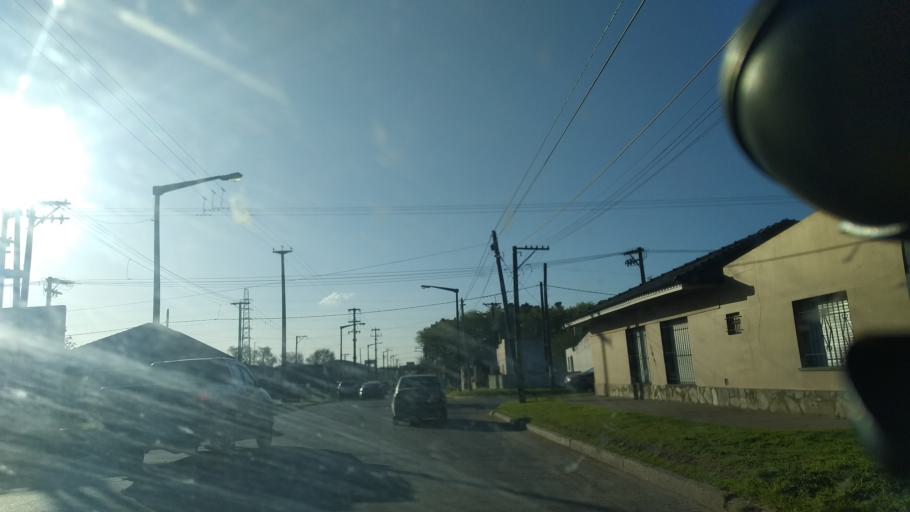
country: AR
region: Buenos Aires
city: Necochea
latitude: -38.5648
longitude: -58.7070
